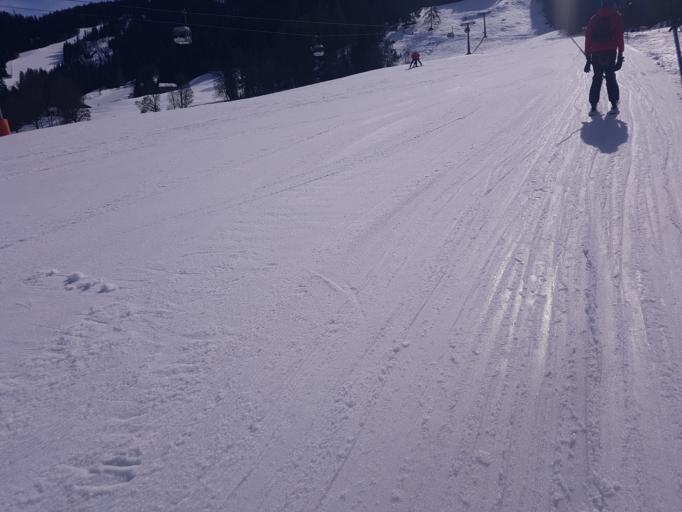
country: AT
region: Tyrol
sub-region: Politischer Bezirk Kufstein
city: Worgl
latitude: 47.4452
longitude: 12.0924
